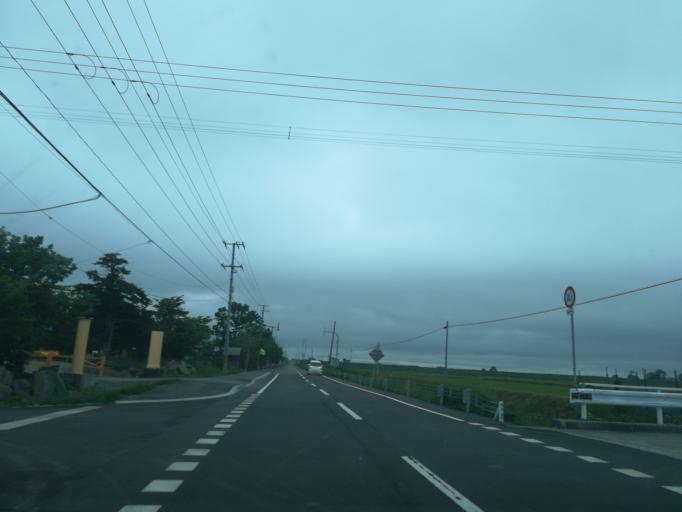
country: JP
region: Hokkaido
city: Iwamizawa
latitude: 43.1252
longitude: 141.6896
